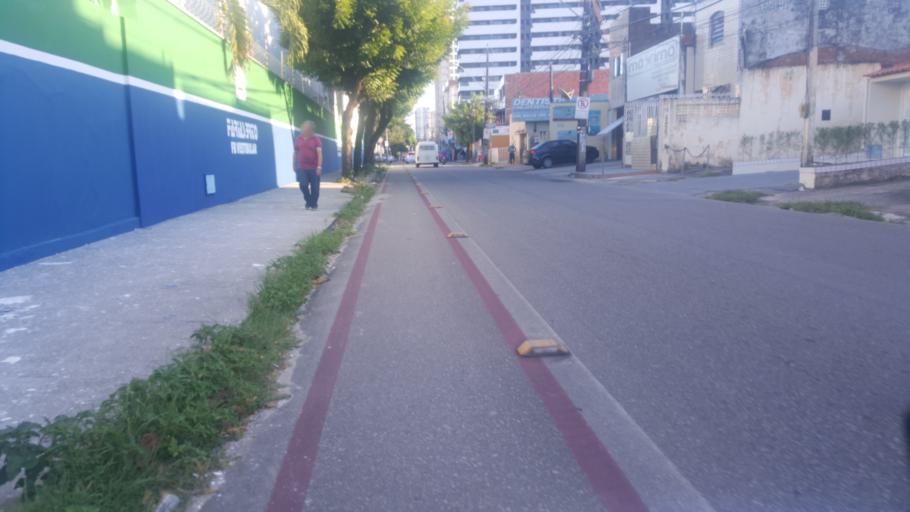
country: BR
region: Ceara
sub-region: Fortaleza
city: Fortaleza
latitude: -3.7384
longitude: -38.5331
